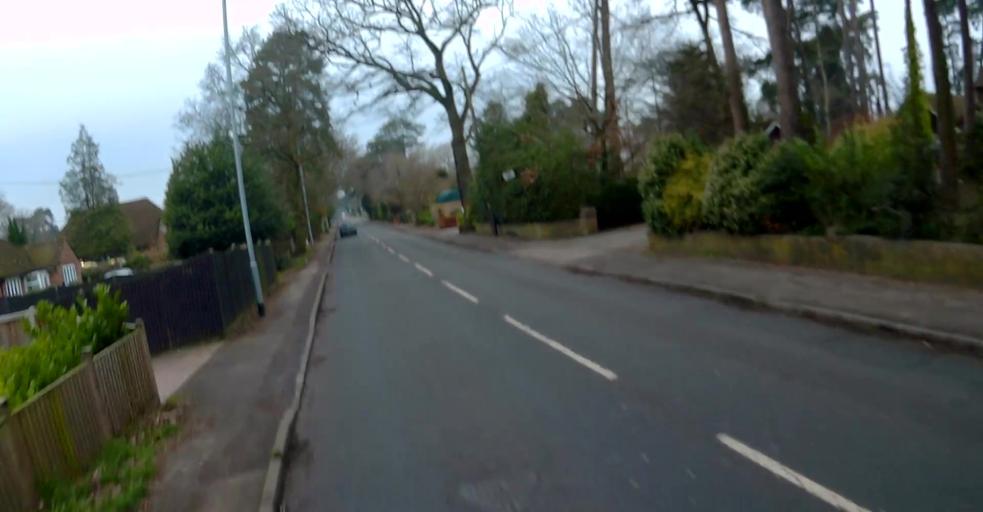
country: GB
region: England
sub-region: Wokingham
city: Finchampstead
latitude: 51.3805
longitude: -0.8555
